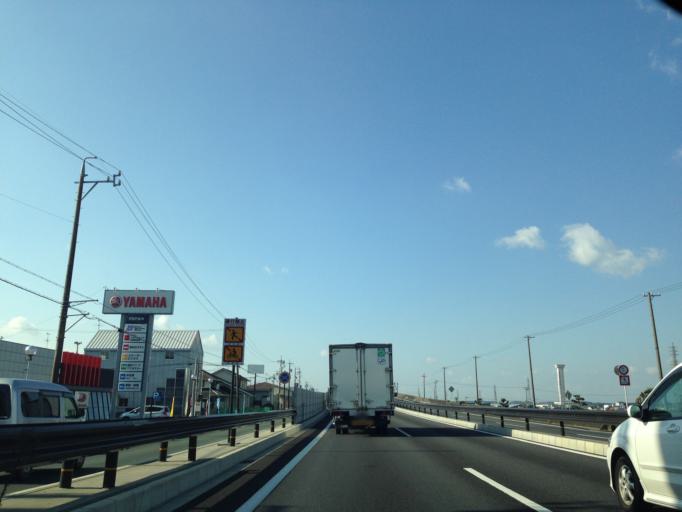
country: JP
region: Shizuoka
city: Fukuroi
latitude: 34.7590
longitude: 137.9409
